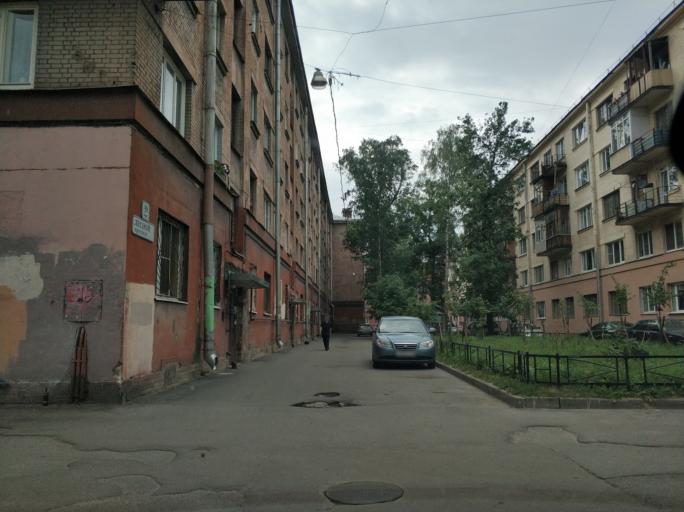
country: RU
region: Leningrad
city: Sampsonievskiy
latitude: 59.9836
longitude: 30.3442
